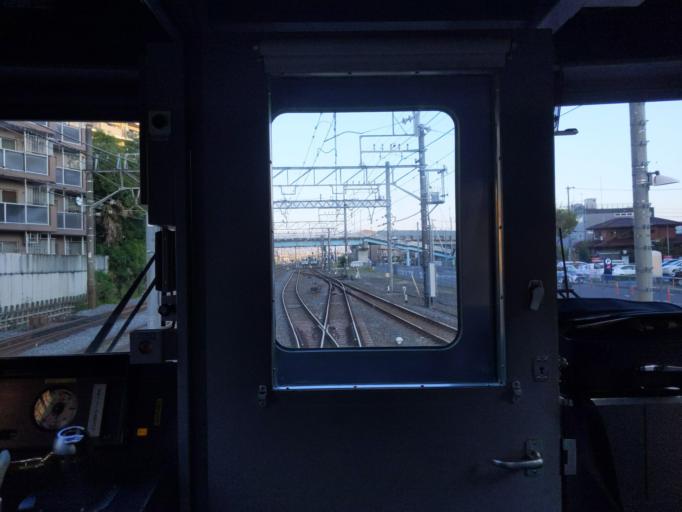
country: JP
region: Saitama
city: Kasukabe
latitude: 35.9786
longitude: 139.7559
